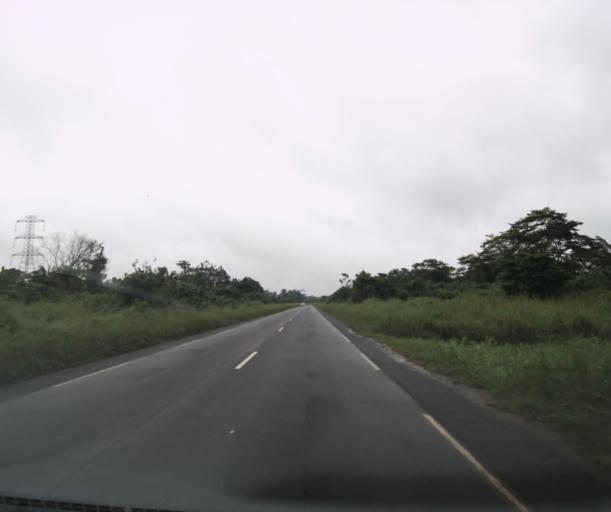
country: CM
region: Littoral
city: Edea
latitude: 3.4831
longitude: 10.1290
